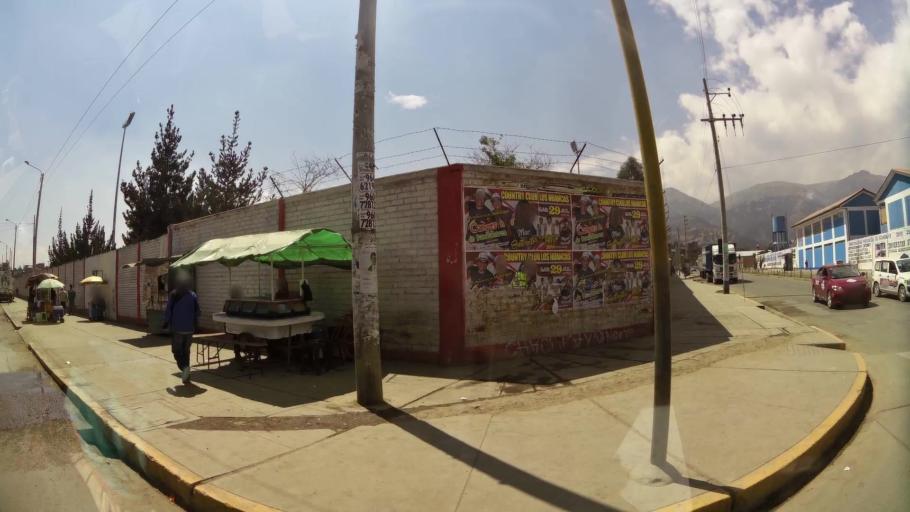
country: PE
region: Junin
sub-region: Provincia de Huancayo
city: Huancayo
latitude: -12.0746
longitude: -75.2021
